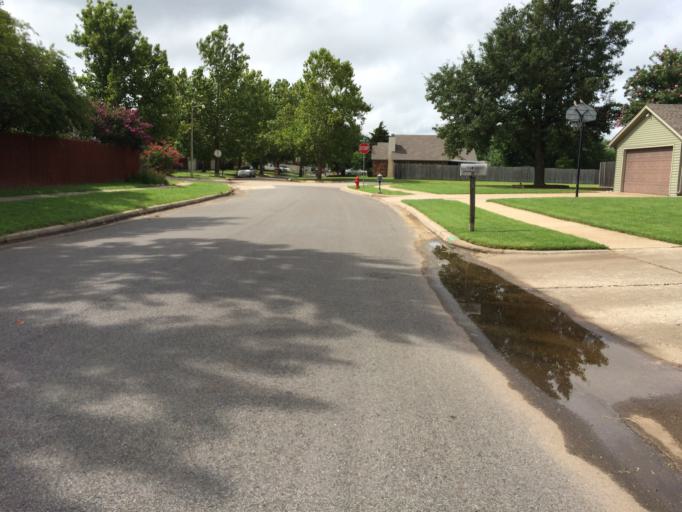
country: US
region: Oklahoma
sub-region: Cleveland County
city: Hall Park
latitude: 35.2224
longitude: -97.4164
